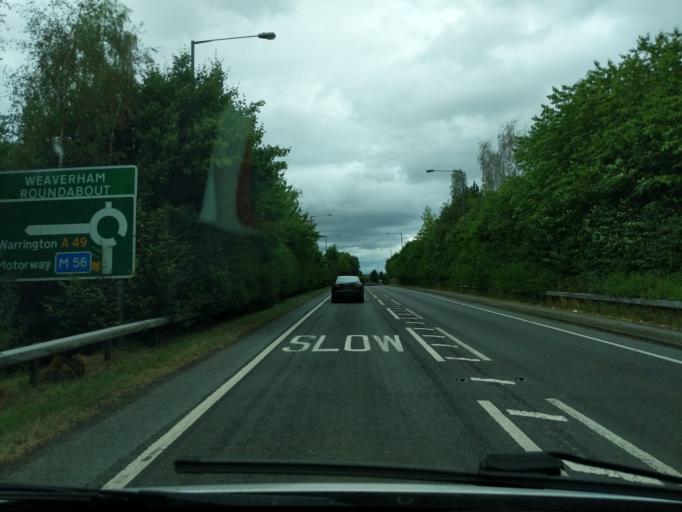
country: GB
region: England
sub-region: Cheshire West and Chester
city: Weaverham
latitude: 53.2576
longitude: -2.5884
